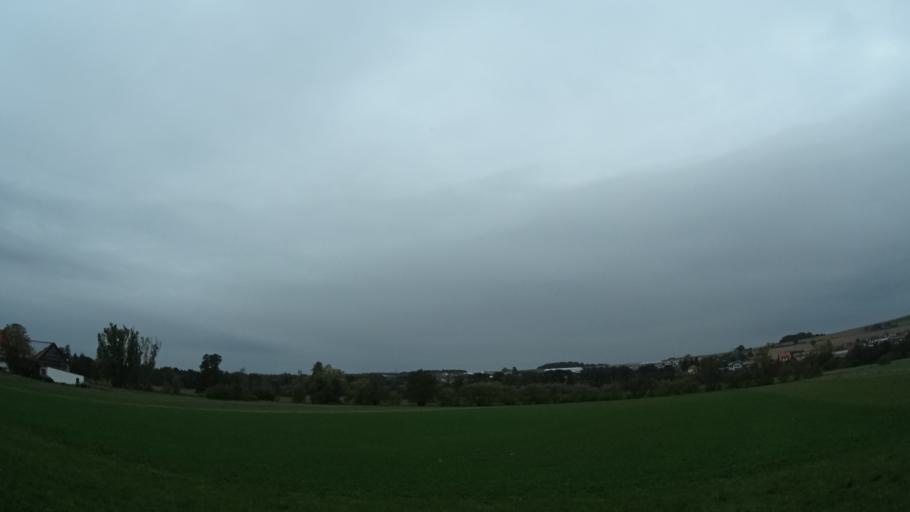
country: DE
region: Hesse
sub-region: Regierungsbezirk Kassel
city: Eichenzell
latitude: 50.4727
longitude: 9.7357
